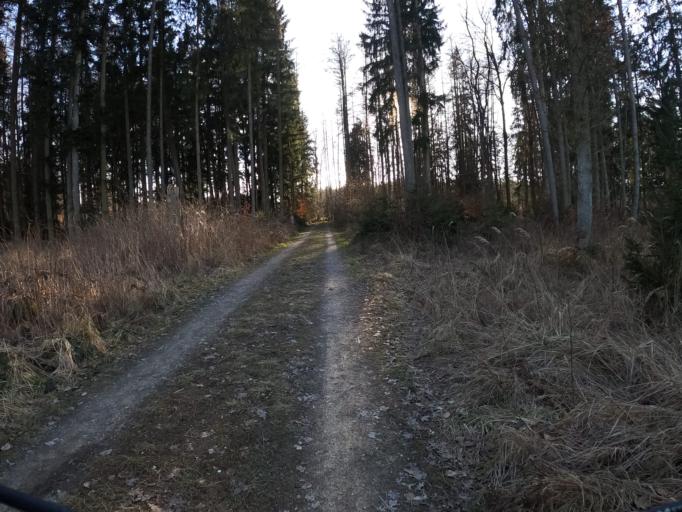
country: DE
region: Bavaria
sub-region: Swabia
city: Leipheim
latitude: 48.4161
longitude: 10.2097
